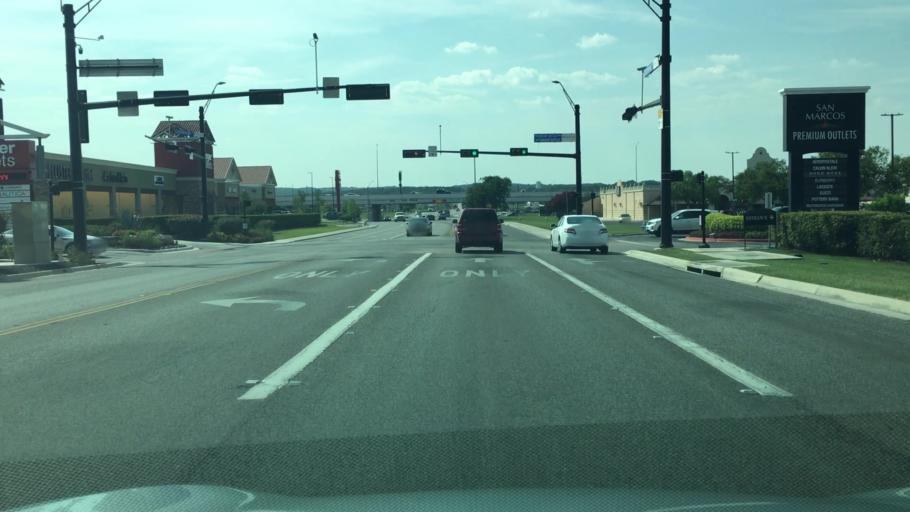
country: US
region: Texas
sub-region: Hays County
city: San Marcos
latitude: 29.8261
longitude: -97.9835
